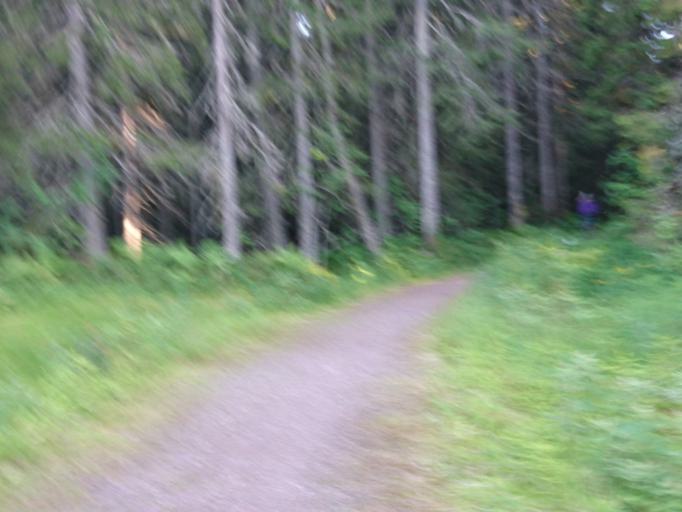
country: SE
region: Dalarna
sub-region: Malung-Saelens kommun
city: Malung
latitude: 61.1694
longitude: 13.1773
